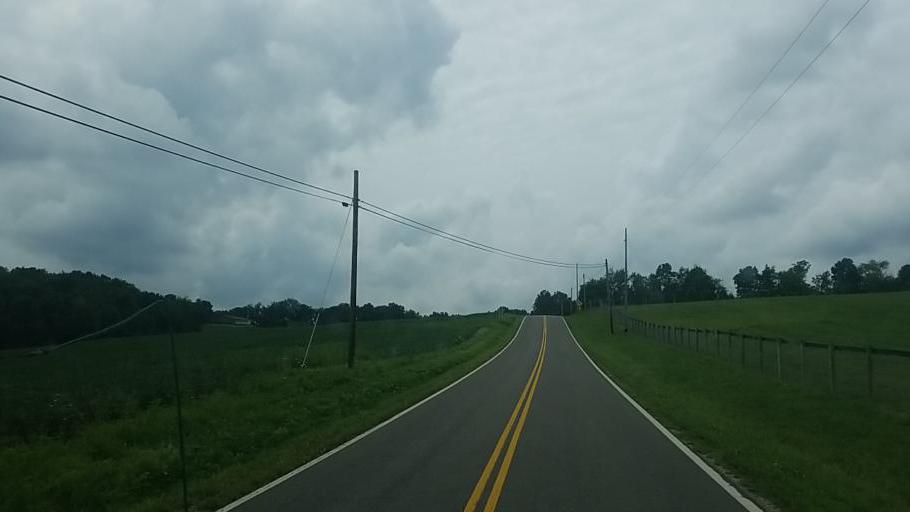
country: US
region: Ohio
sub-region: Licking County
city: Utica
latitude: 40.2198
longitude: -82.3729
